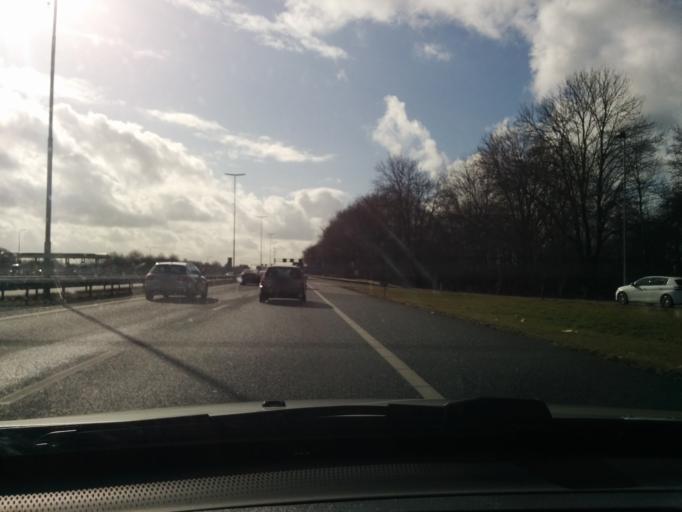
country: NL
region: Utrecht
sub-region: Gemeente De Bilt
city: De Bilt
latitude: 52.1306
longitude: 5.1507
